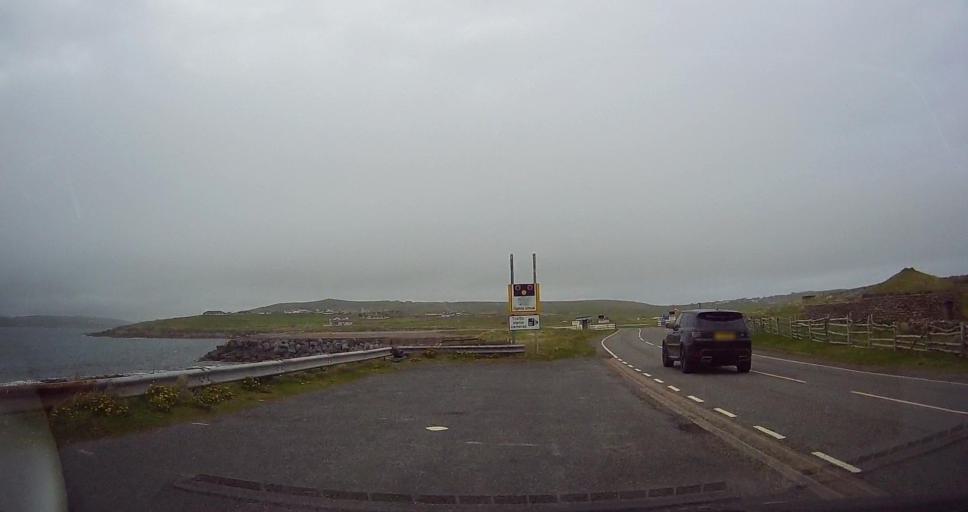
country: GB
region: Scotland
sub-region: Shetland Islands
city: Sandwick
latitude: 59.8786
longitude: -1.3069
